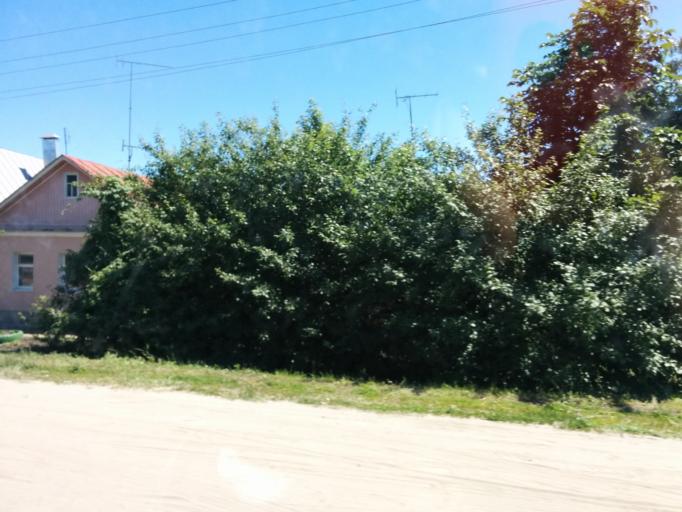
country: RU
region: Tambov
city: Morshansk
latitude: 53.4328
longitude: 41.7978
